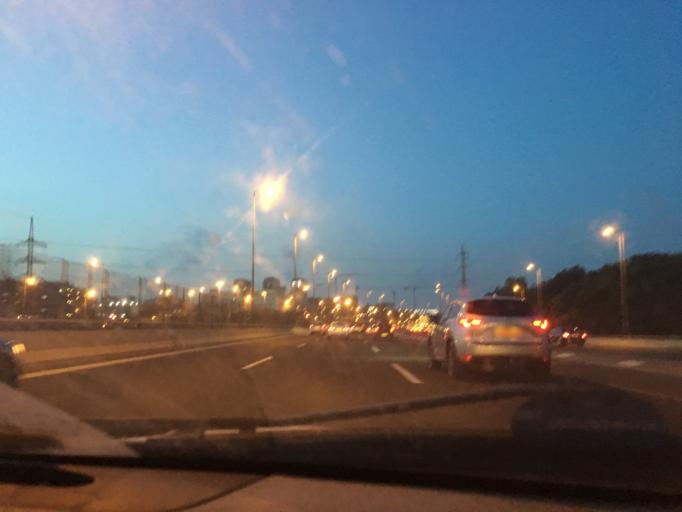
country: IL
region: Tel Aviv
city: Ramat Gan
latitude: 32.0994
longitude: 34.8028
